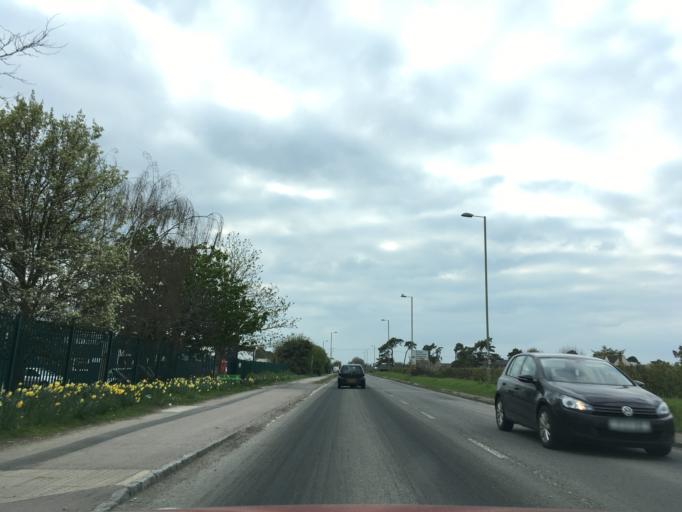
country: GB
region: England
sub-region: Oxfordshire
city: Witney
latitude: 51.7930
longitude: -1.5183
